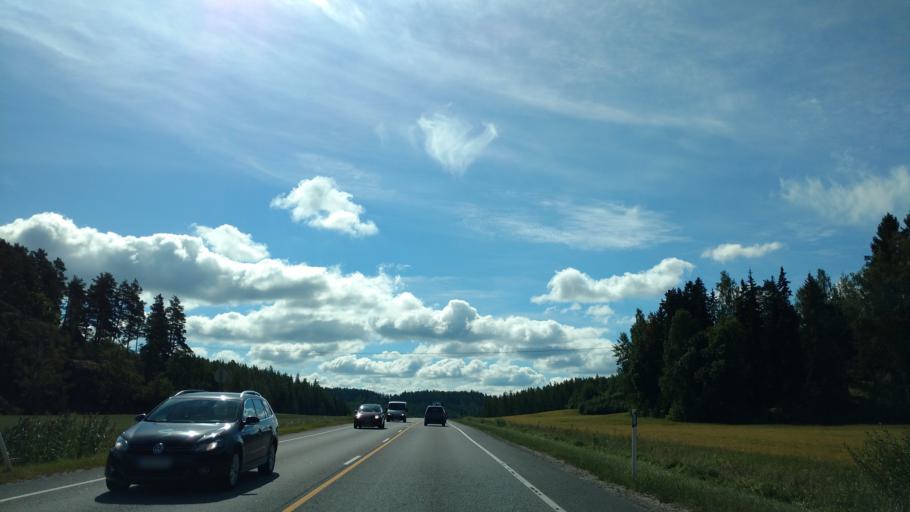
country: FI
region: Varsinais-Suomi
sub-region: Salo
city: Salo
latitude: 60.3667
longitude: 23.1381
